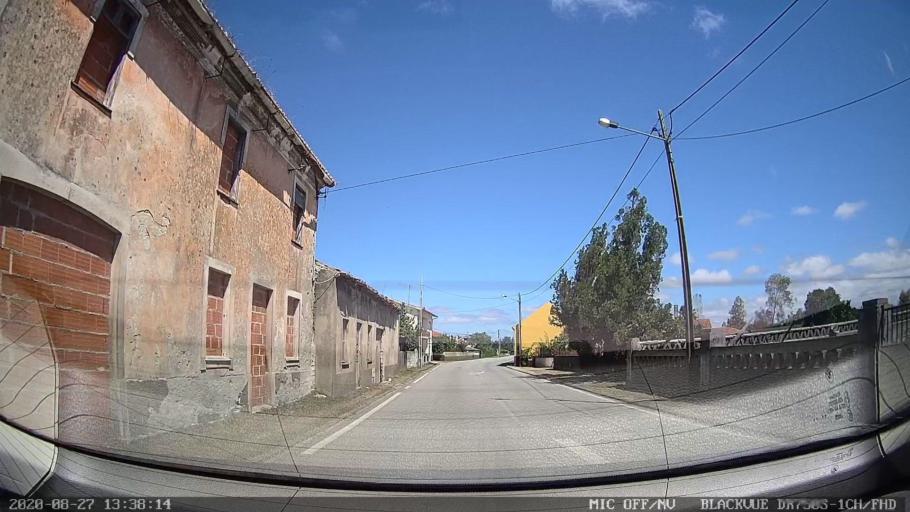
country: PT
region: Coimbra
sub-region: Mira
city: Mira
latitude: 40.4475
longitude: -8.7225
